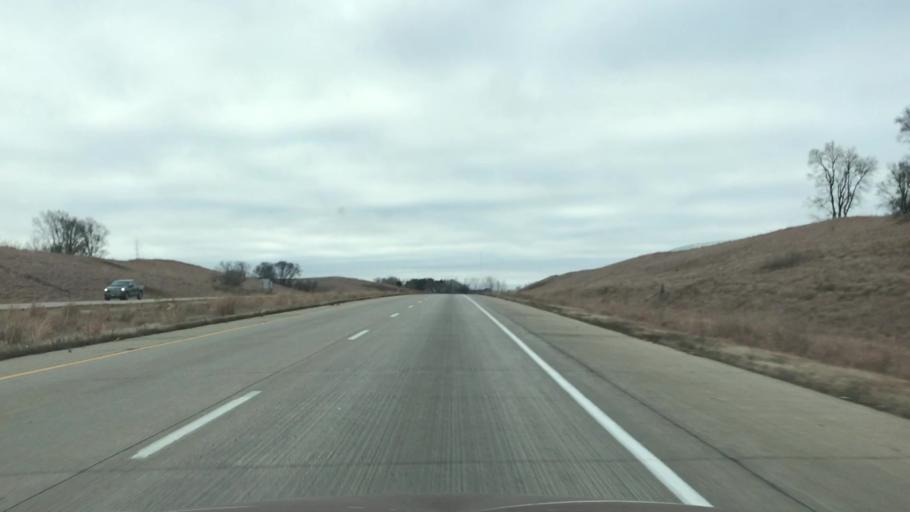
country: US
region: Iowa
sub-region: Woodbury County
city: Sioux City
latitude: 42.5043
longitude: -96.3246
